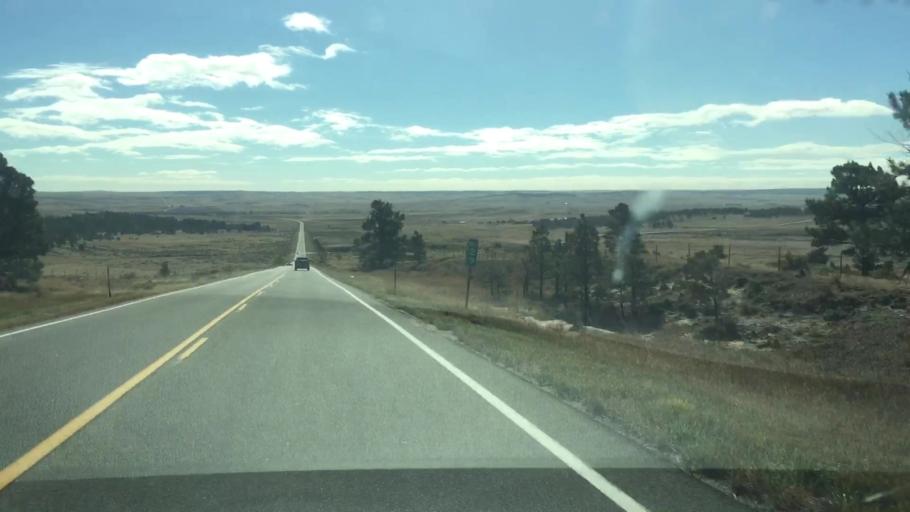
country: US
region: Colorado
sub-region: Elbert County
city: Kiowa
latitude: 39.3124
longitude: -104.3643
